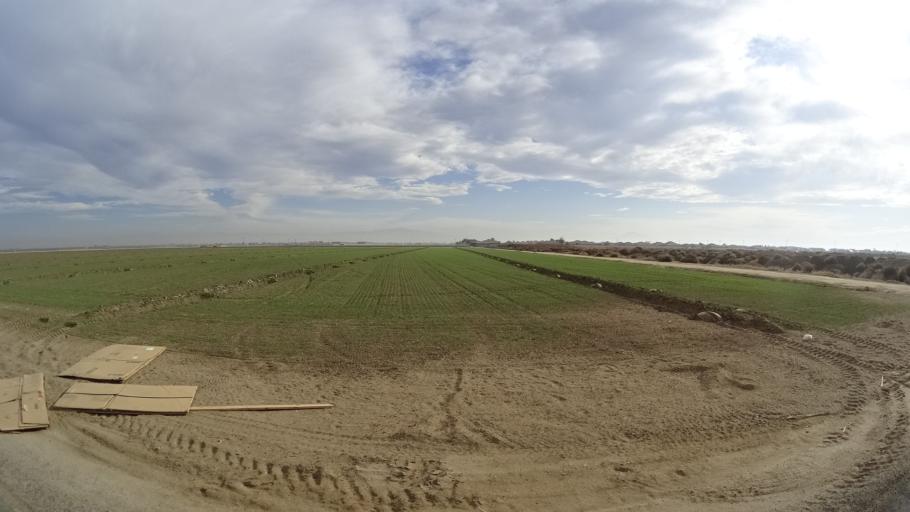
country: US
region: California
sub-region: Kern County
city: Rosedale
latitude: 35.4088
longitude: -119.1721
